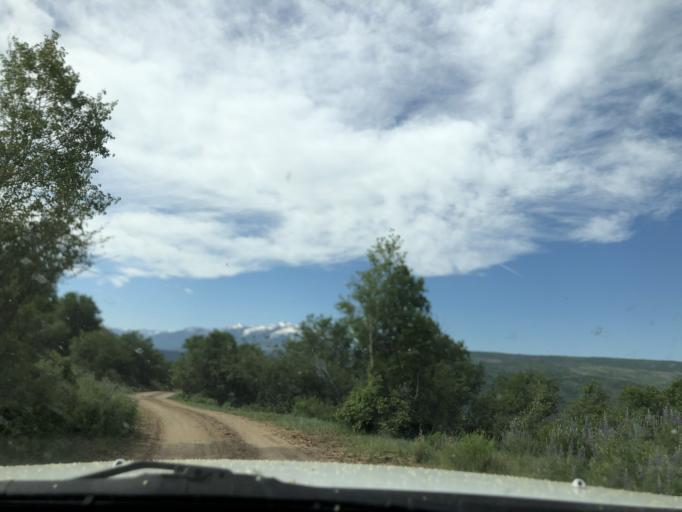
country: US
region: Colorado
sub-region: Delta County
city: Paonia
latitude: 39.0113
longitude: -107.3419
